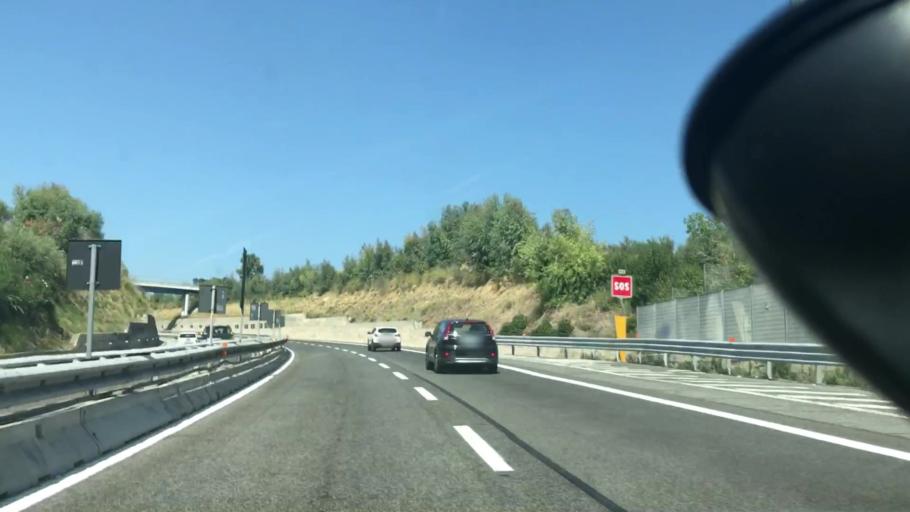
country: IT
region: Abruzzo
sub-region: Provincia di Chieti
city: San Vito Chietino
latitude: 42.2974
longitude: 14.4322
